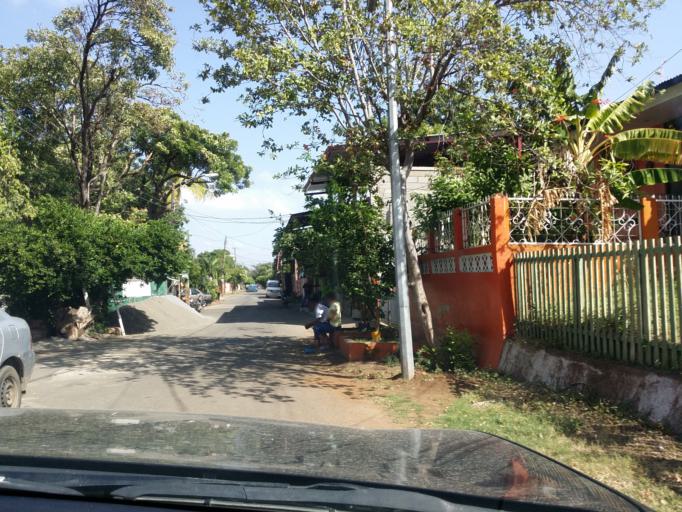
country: NI
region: Managua
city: Managua
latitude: 12.1267
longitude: -86.2313
